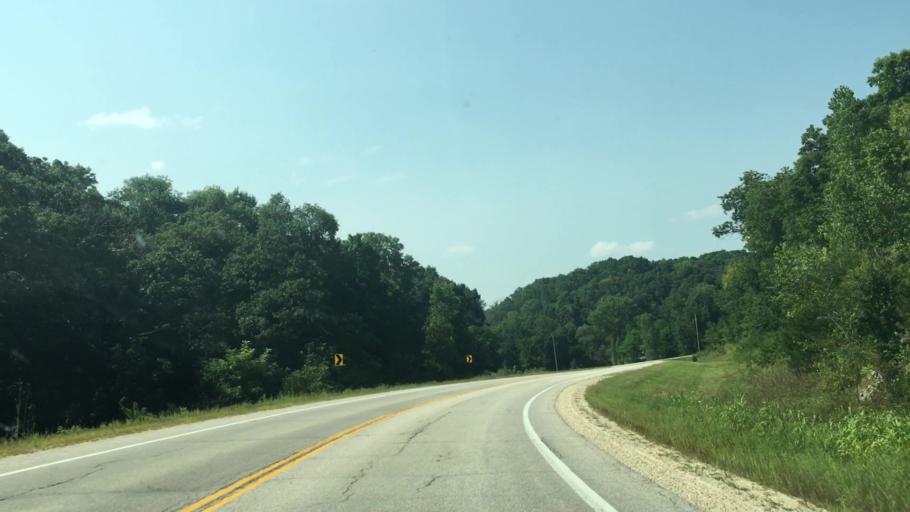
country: US
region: Minnesota
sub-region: Fillmore County
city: Preston
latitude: 43.6985
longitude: -91.9644
